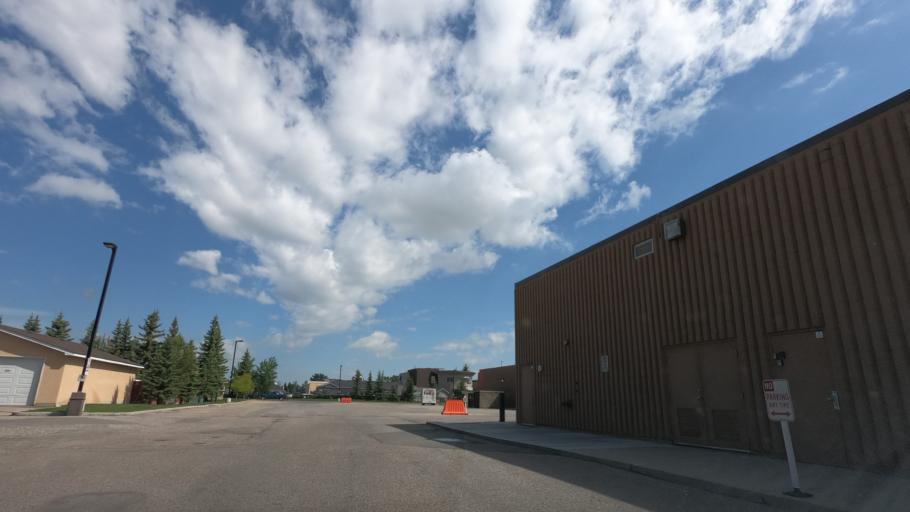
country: CA
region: Alberta
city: Airdrie
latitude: 51.2890
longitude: -114.0160
